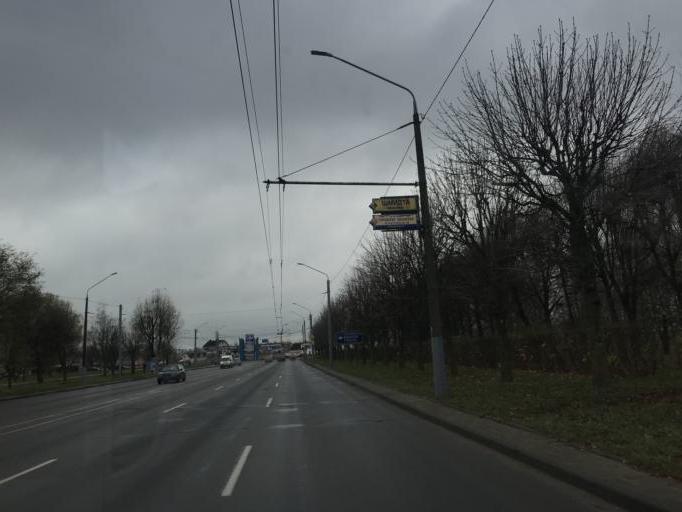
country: BY
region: Mogilev
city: Mahilyow
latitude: 53.8633
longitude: 30.3346
